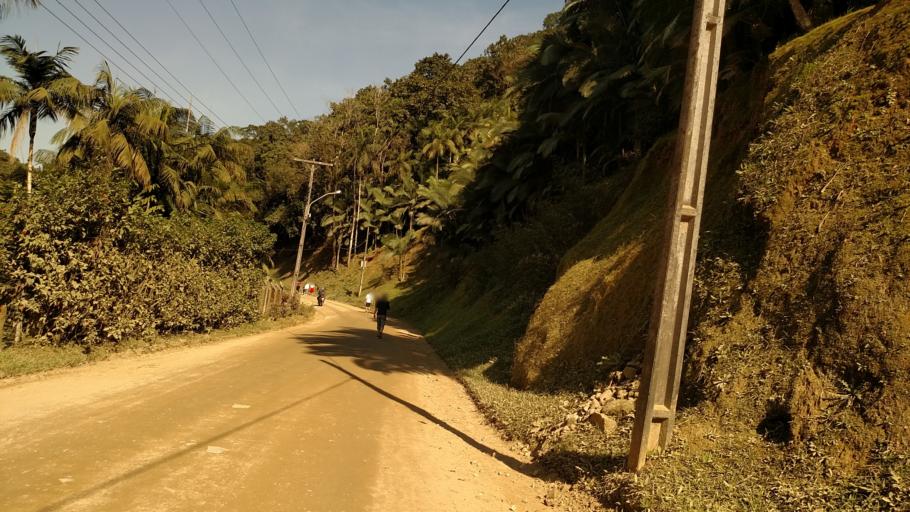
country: BR
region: Santa Catarina
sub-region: Pomerode
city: Pomerode
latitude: -26.7335
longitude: -49.0717
